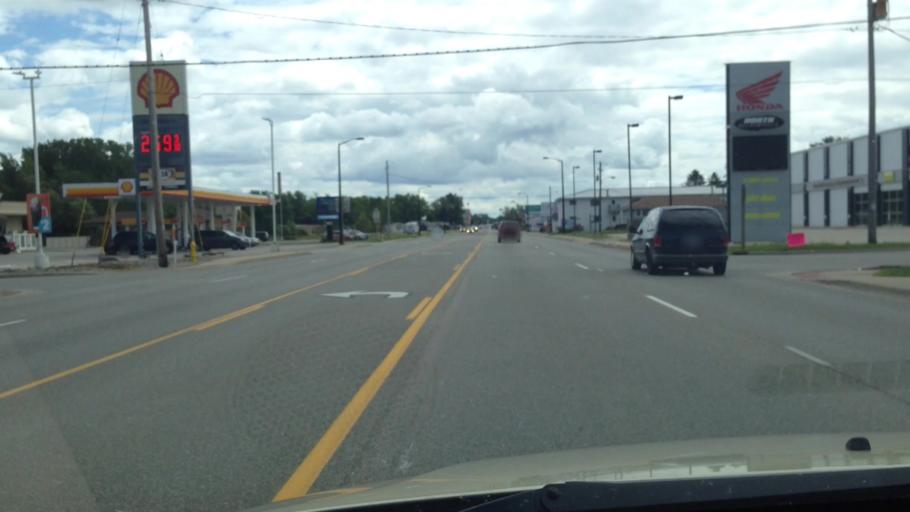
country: US
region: Michigan
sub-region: Menominee County
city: Menominee
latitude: 45.1335
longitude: -87.6126
